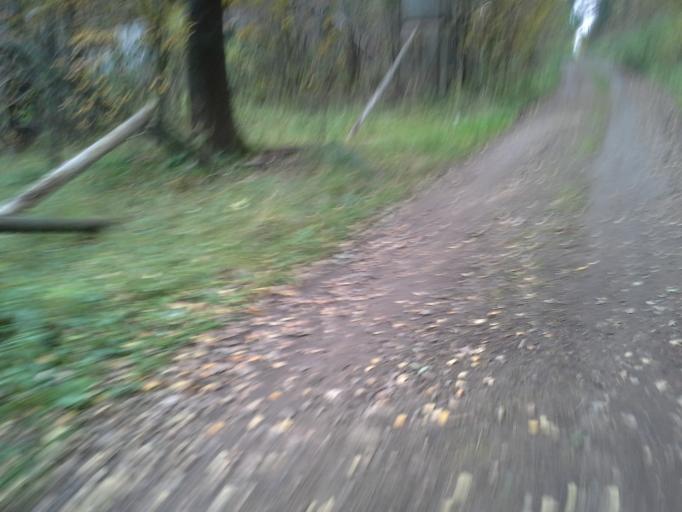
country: RU
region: Moskovskaya
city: Nazar'yevo
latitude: 55.6911
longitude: 37.0151
